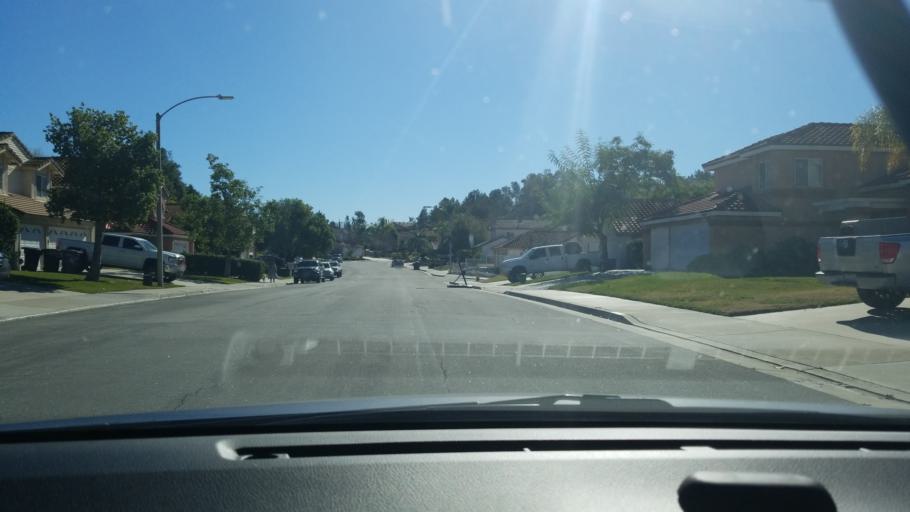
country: US
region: California
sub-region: Riverside County
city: Temecula
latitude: 33.5330
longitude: -117.1082
